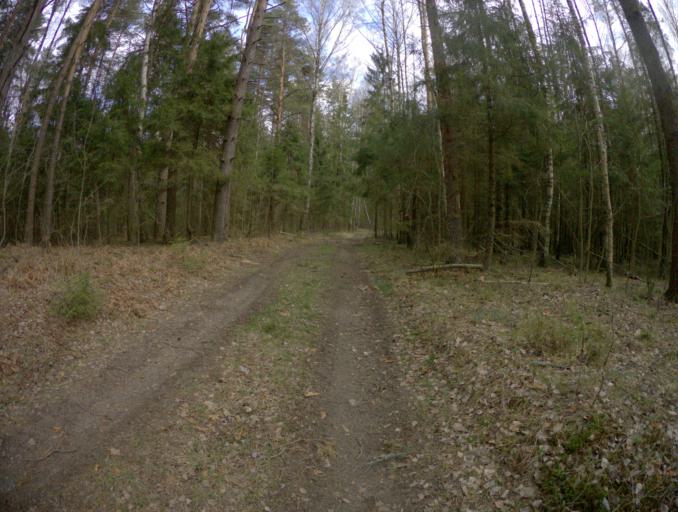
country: RU
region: Vladimir
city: Orgtrud
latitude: 56.0713
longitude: 40.6976
